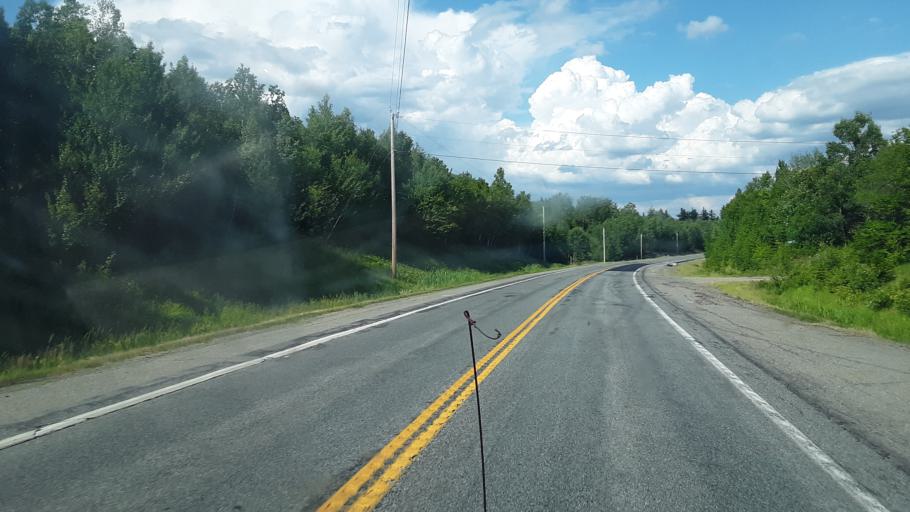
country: US
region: Maine
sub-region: Washington County
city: Cherryfield
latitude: 44.8715
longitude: -67.9945
